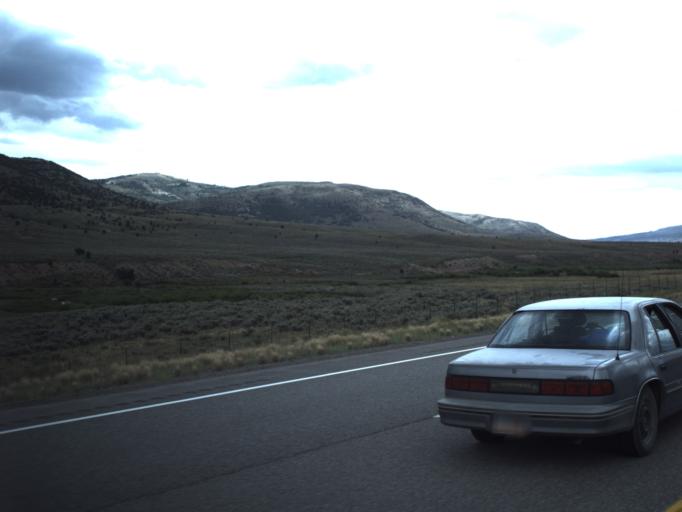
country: US
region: Utah
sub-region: Carbon County
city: Helper
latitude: 39.9077
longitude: -111.0603
